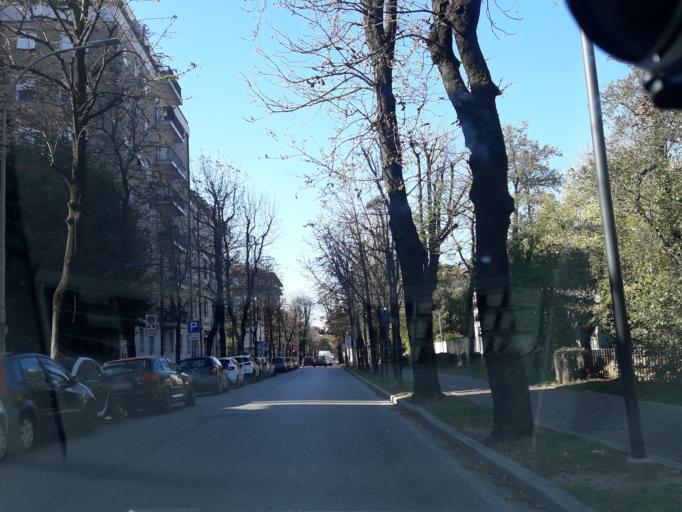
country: IT
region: Friuli Venezia Giulia
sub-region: Provincia di Udine
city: Udine
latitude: 46.0580
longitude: 13.2400
